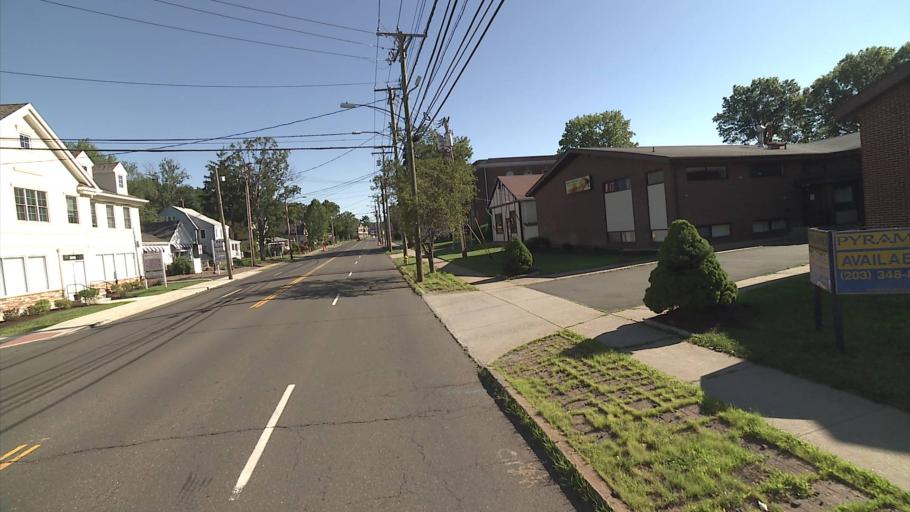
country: US
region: Connecticut
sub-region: New Haven County
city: Hamden
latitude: 41.3860
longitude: -72.9009
